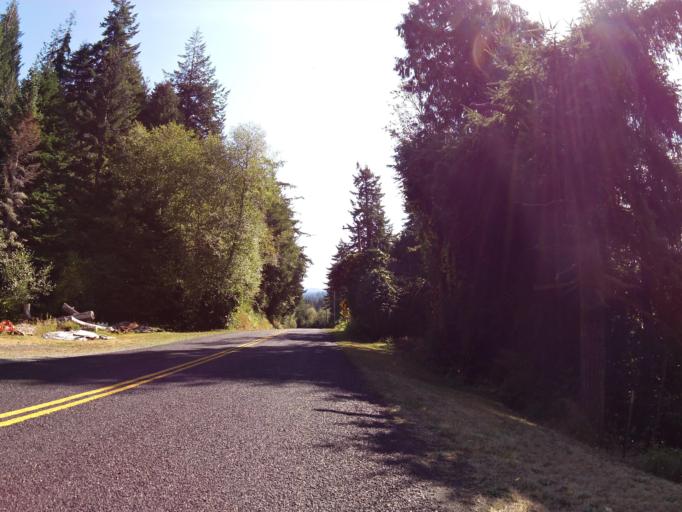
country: US
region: Washington
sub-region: Wahkiakum County
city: Cathlamet
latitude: 46.1857
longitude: -123.5810
